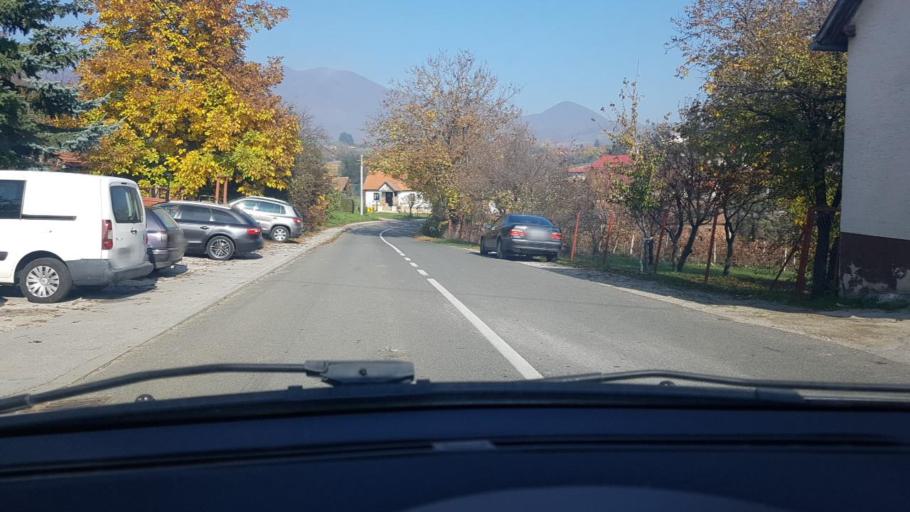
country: HR
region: Krapinsko-Zagorska
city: Zlatar
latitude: 46.1343
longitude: 16.1227
